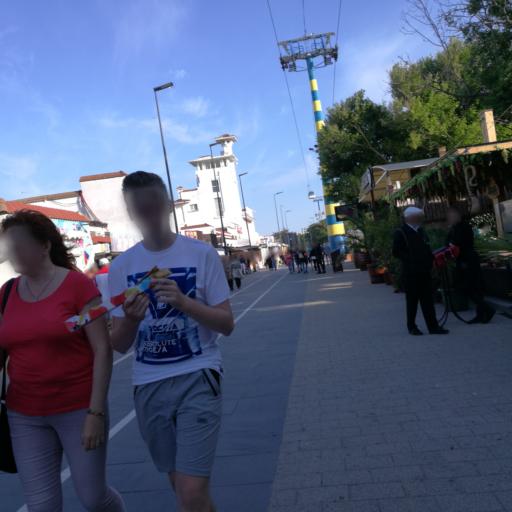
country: RO
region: Constanta
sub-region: Municipiul Constanta
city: Palazu Mare
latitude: 44.2362
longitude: 28.6254
